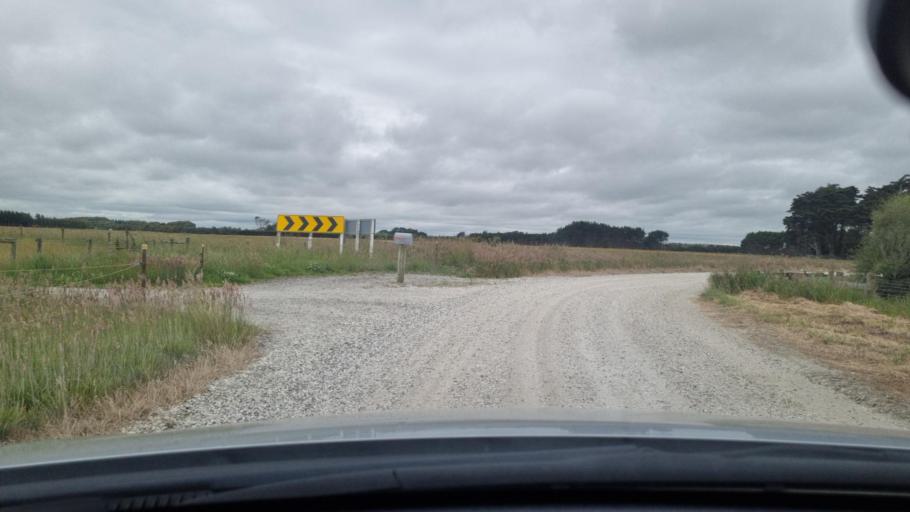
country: NZ
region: Southland
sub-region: Invercargill City
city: Invercargill
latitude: -46.3787
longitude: 168.2882
